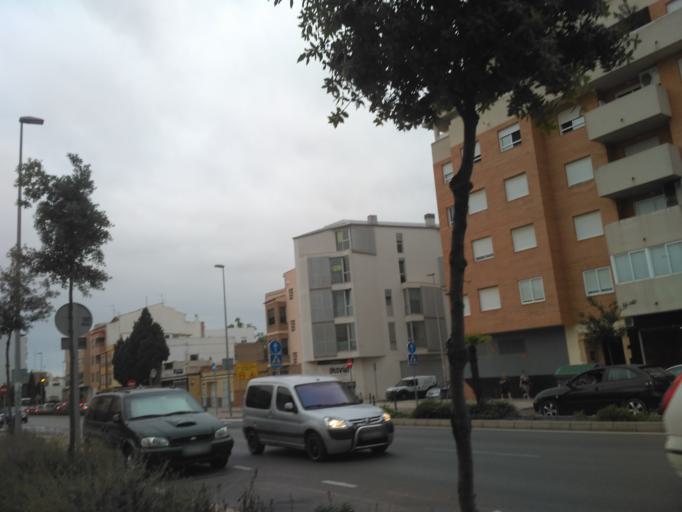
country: ES
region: Valencia
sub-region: Provincia de Castello
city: Castello de la Plana
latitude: 39.9864
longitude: -0.0555
